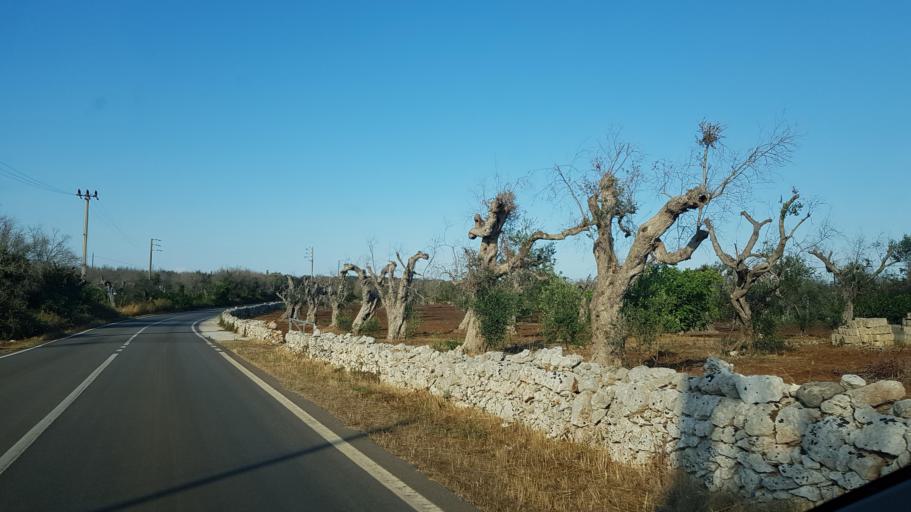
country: IT
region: Apulia
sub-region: Provincia di Lecce
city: Castiglione
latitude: 39.9848
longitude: 18.3557
